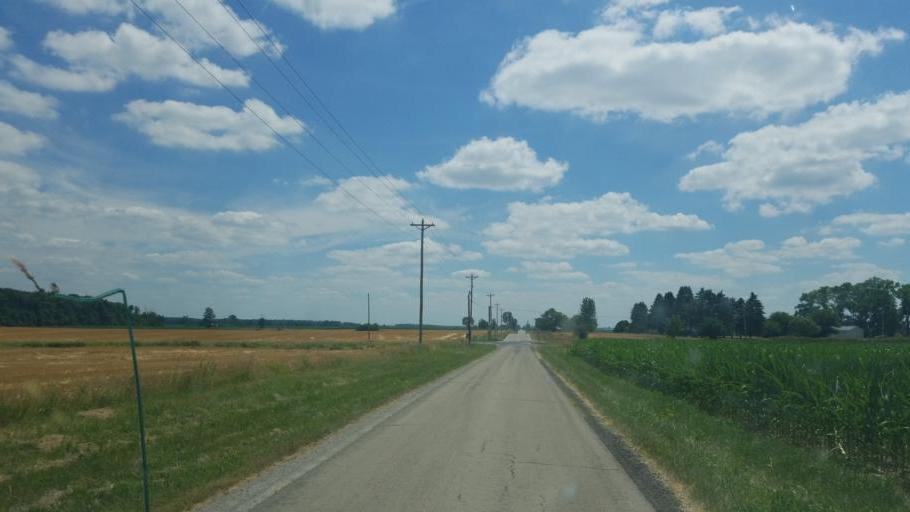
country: US
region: Ohio
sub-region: Defiance County
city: Hicksville
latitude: 41.3386
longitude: -84.6900
